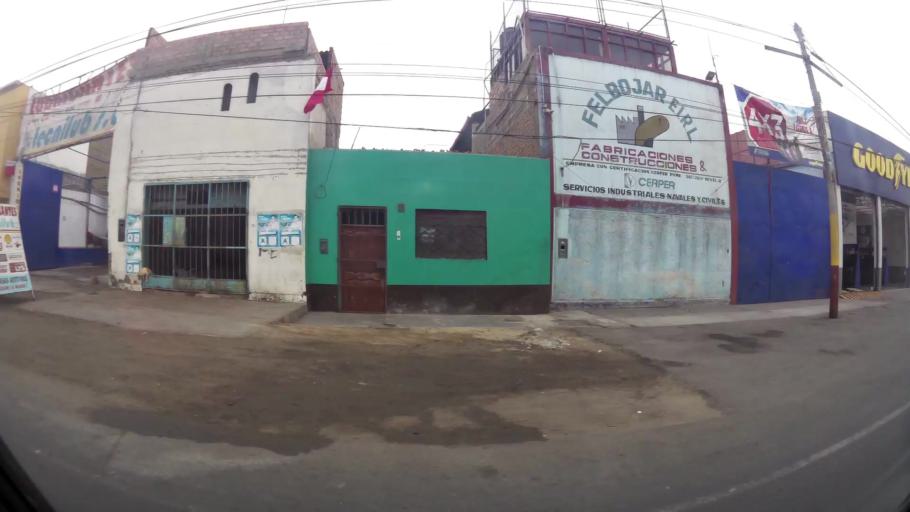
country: PE
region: Ancash
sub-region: Provincia de Santa
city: Chimbote
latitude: -9.0831
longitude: -78.5787
